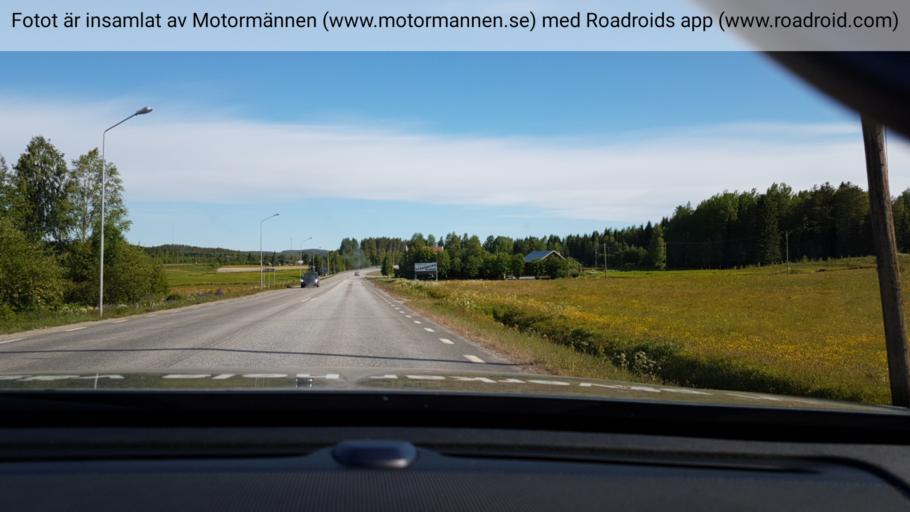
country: SE
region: Vaesterbotten
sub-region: Vannas Kommun
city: Vaennaes
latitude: 63.9806
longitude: 19.7302
